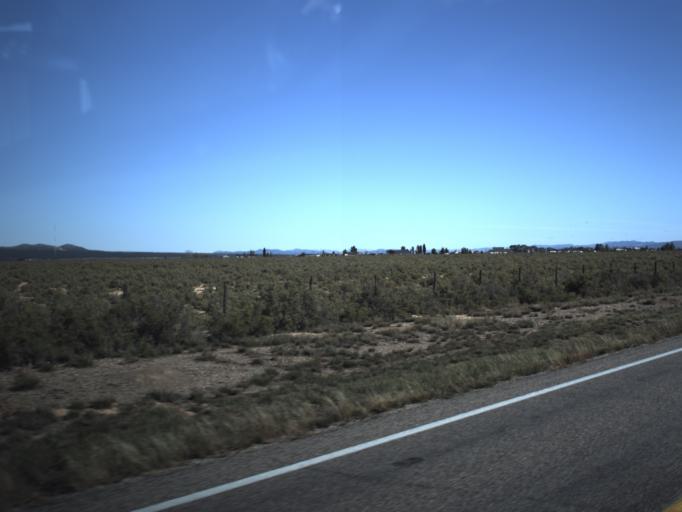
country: US
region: Utah
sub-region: Iron County
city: Cedar City
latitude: 37.6743
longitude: -113.1840
